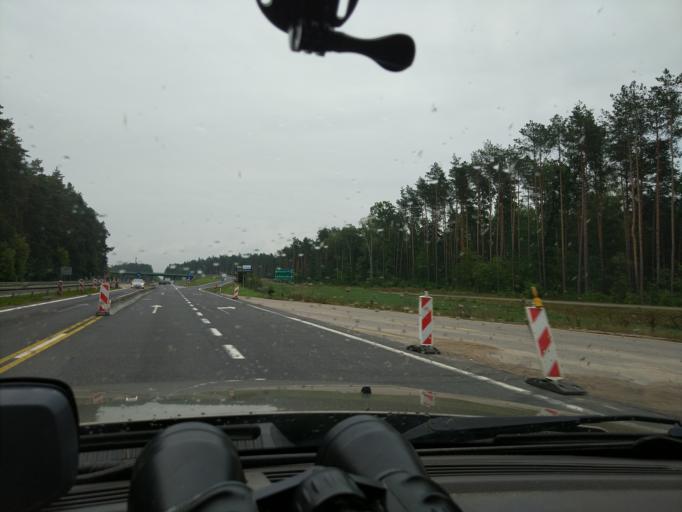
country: PL
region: Masovian Voivodeship
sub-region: Powiat ostrowski
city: Ostrow Mazowiecka
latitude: 52.7824
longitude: 21.8543
